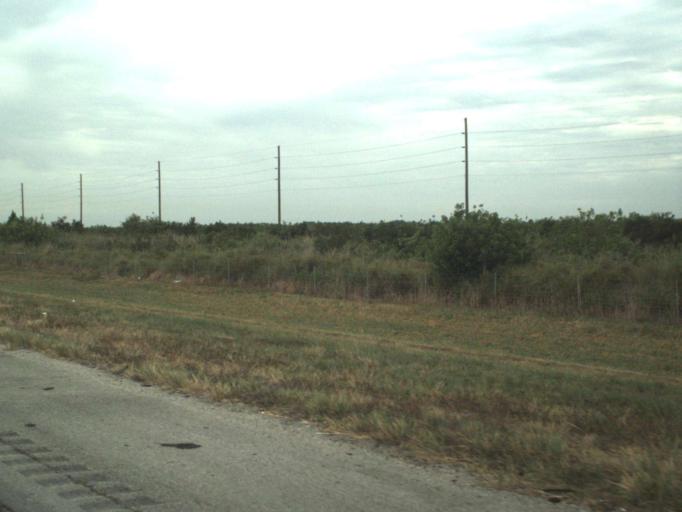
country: US
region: Florida
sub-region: Saint Lucie County
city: Port Saint Lucie
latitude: 27.1978
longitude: -80.4007
